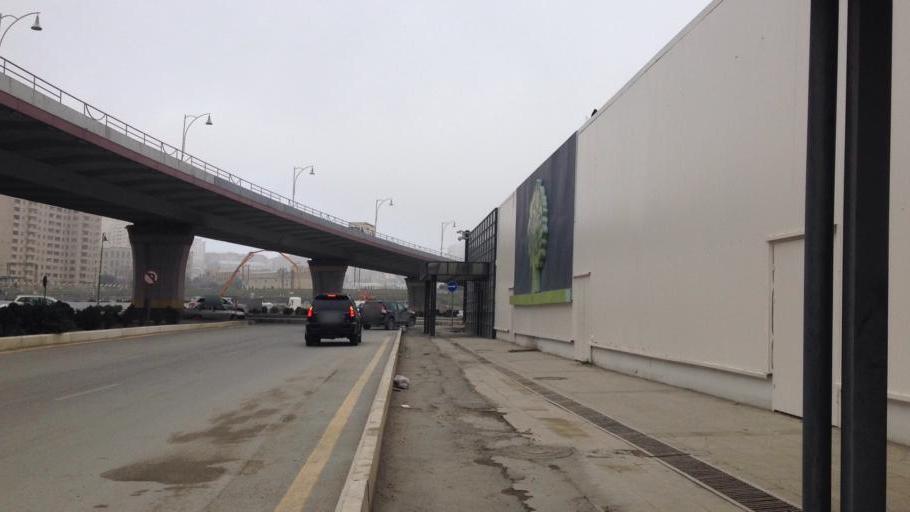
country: AZ
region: Baki
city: Baku
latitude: 40.3879
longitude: 49.8665
